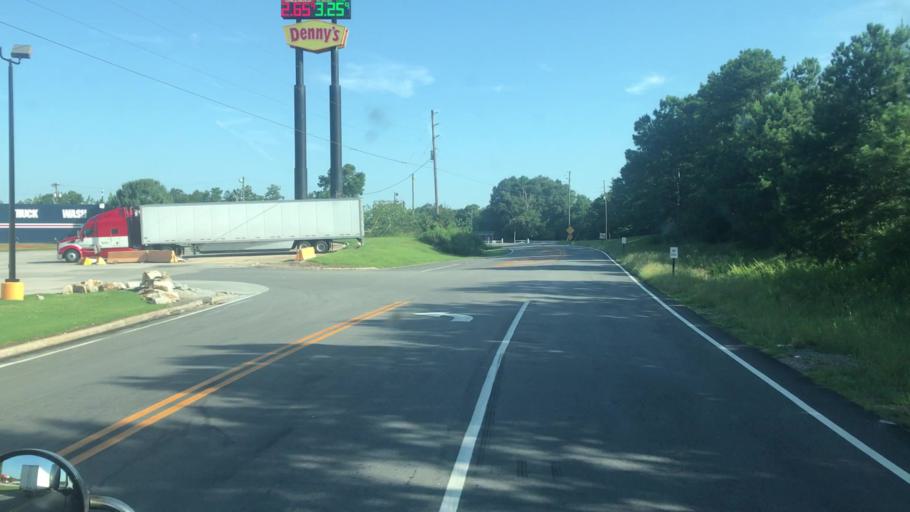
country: US
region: Georgia
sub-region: Butts County
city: Jackson
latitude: 33.2080
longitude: -84.0631
